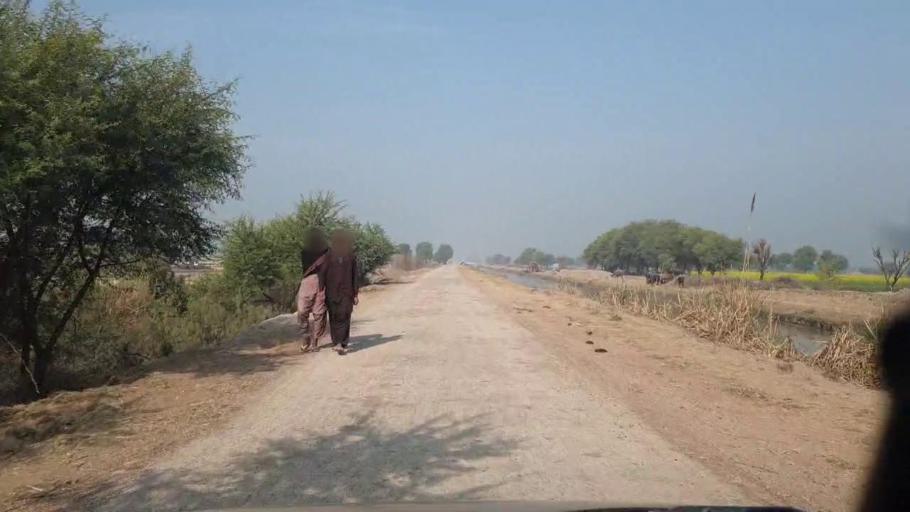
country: PK
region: Sindh
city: Shahdadpur
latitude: 26.0362
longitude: 68.5318
